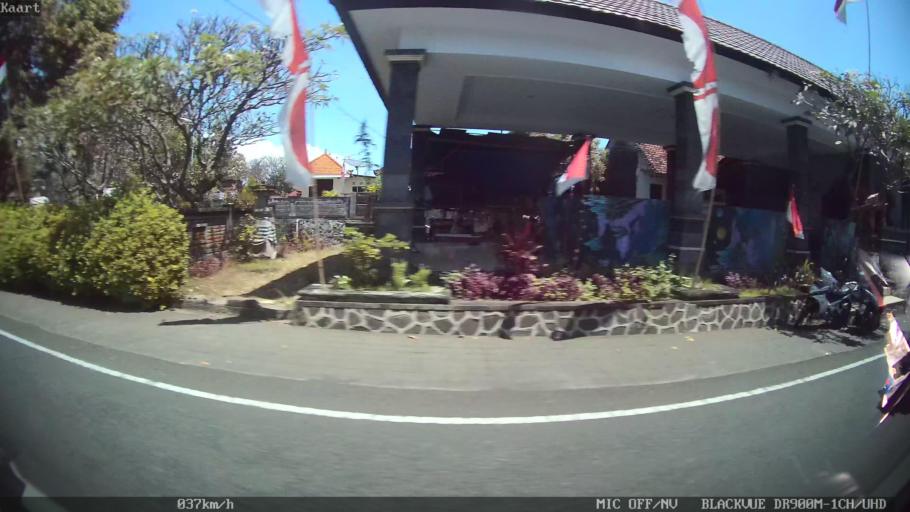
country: ID
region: Bali
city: Banjar Beratan
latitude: -8.1331
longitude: 115.1000
